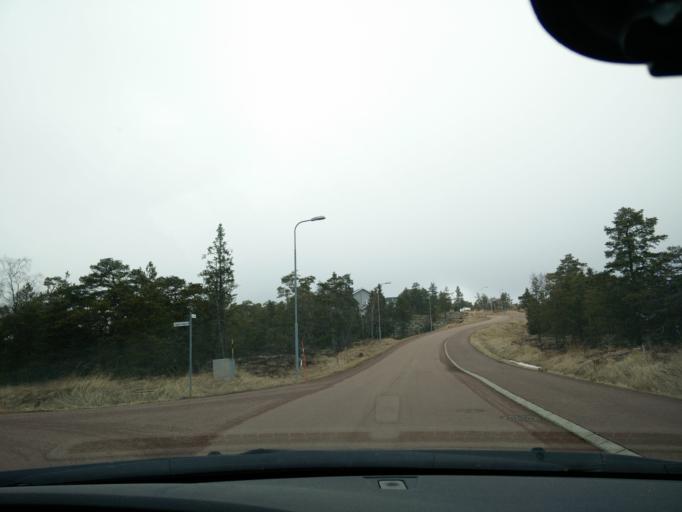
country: AX
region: Alands landsbygd
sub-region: Jomala
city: Jomala
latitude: 60.1283
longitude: 19.9285
